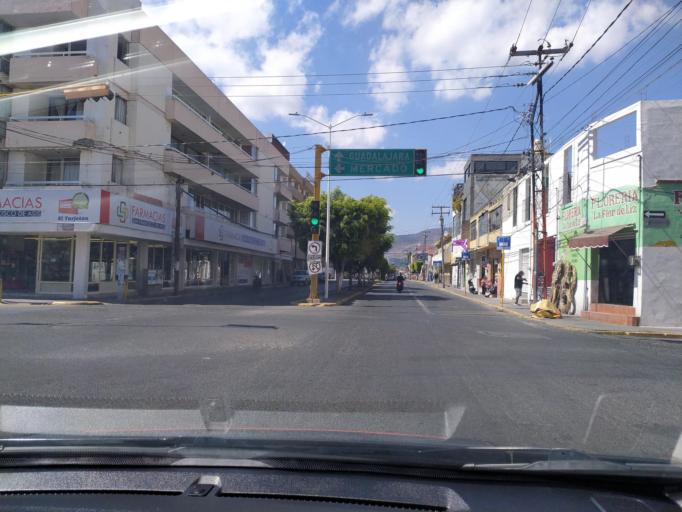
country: LA
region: Oudomxai
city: Muang La
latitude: 21.0153
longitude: 101.8598
